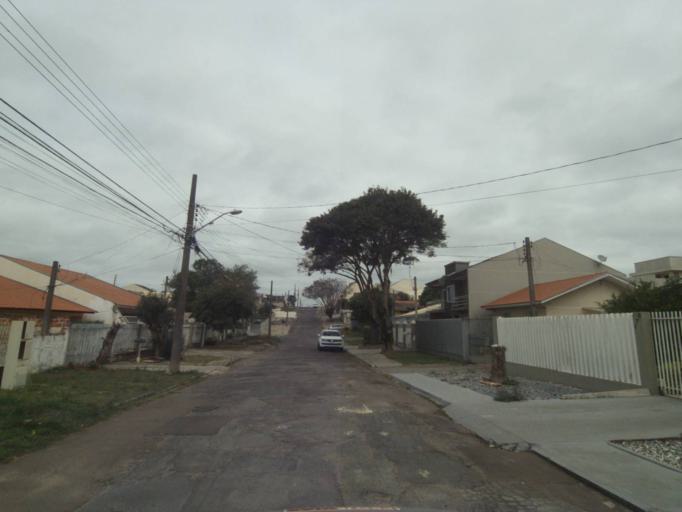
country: BR
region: Parana
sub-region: Pinhais
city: Pinhais
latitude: -25.4796
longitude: -49.2303
